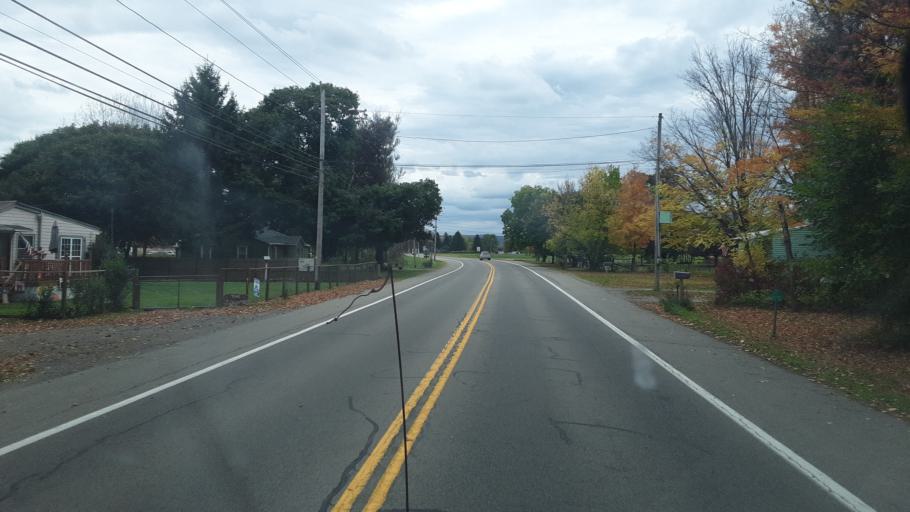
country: US
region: New York
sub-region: Allegany County
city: Belmont
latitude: 42.2133
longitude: -78.0197
